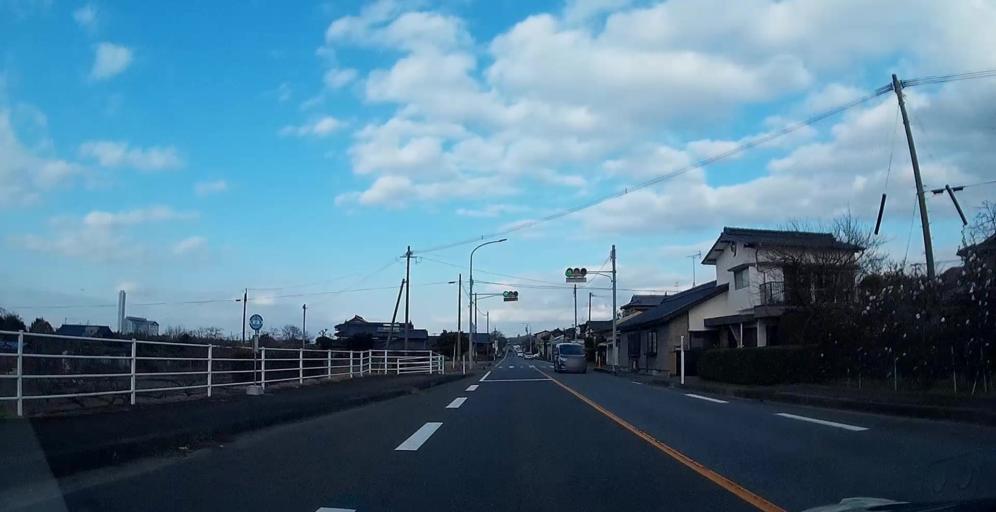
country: JP
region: Kumamoto
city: Yatsushiro
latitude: 32.5394
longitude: 130.6718
